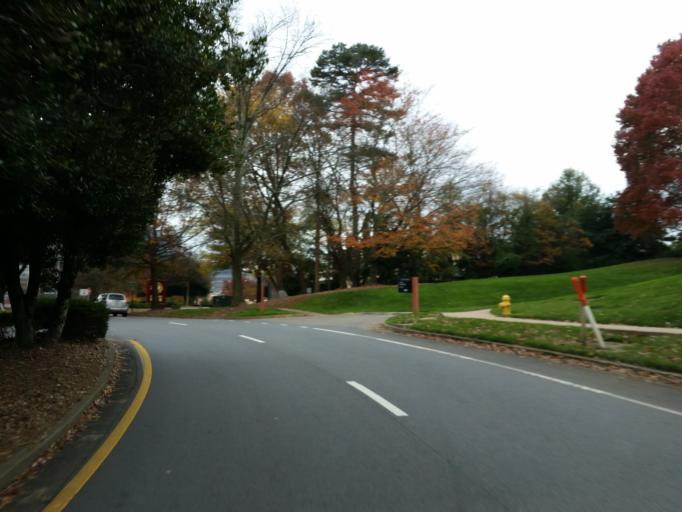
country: US
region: Georgia
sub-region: DeKalb County
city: Dunwoody
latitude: 33.9306
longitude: -84.3460
